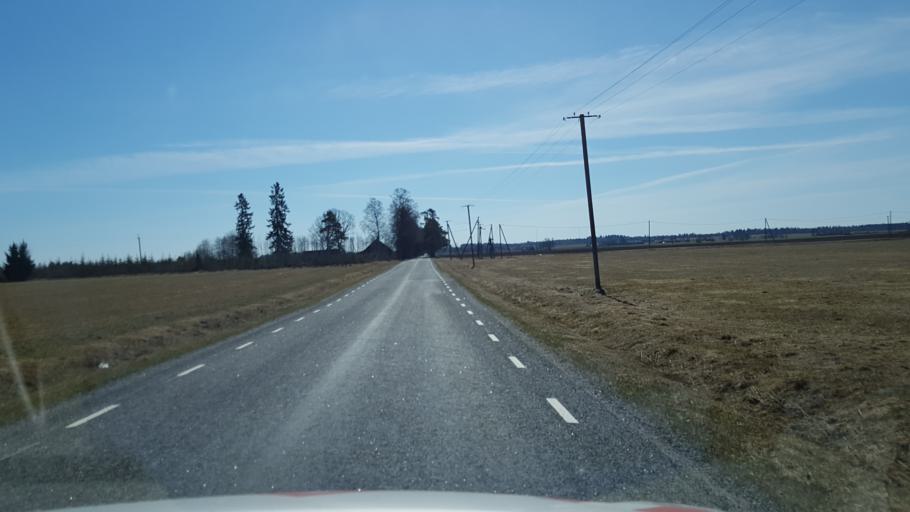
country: EE
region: Laeaene-Virumaa
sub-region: Vinni vald
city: Vinni
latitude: 59.1208
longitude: 26.5225
